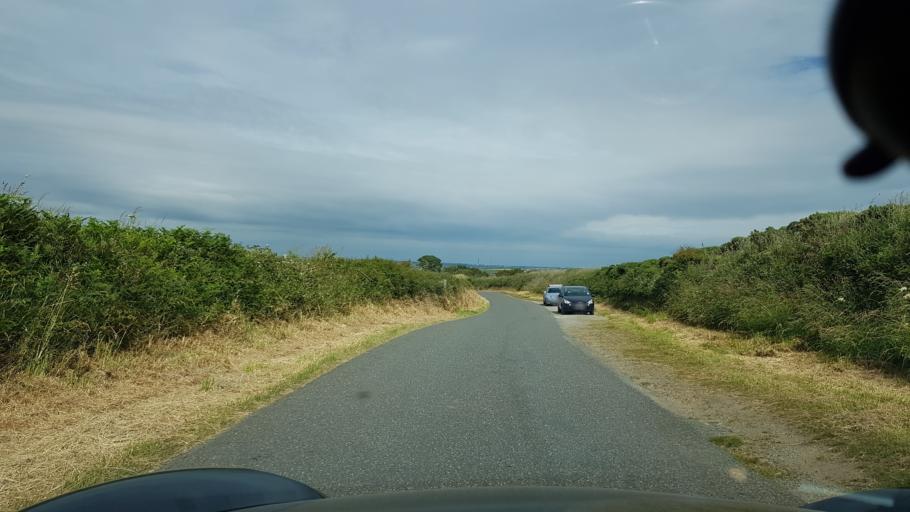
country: GB
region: Wales
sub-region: Pembrokeshire
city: Dale
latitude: 51.7317
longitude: -5.2073
